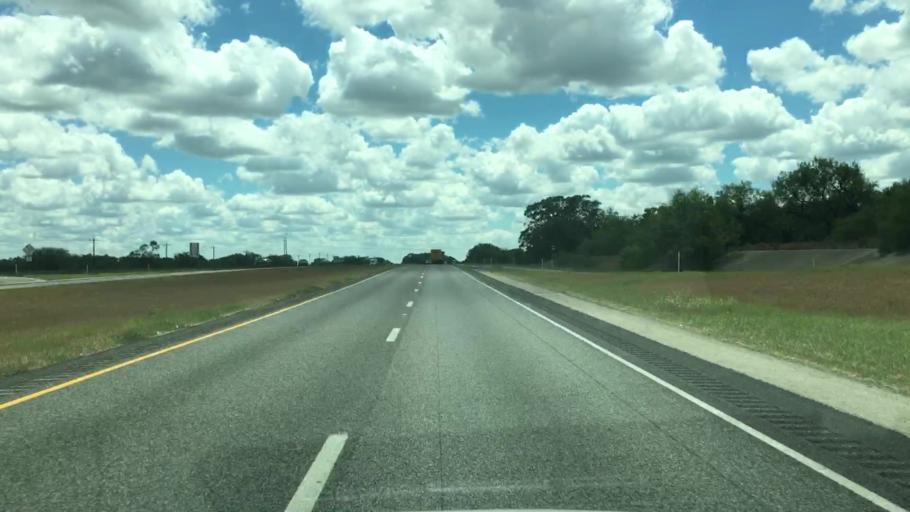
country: US
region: Texas
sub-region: Atascosa County
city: Pleasanton
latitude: 28.9445
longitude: -98.4368
